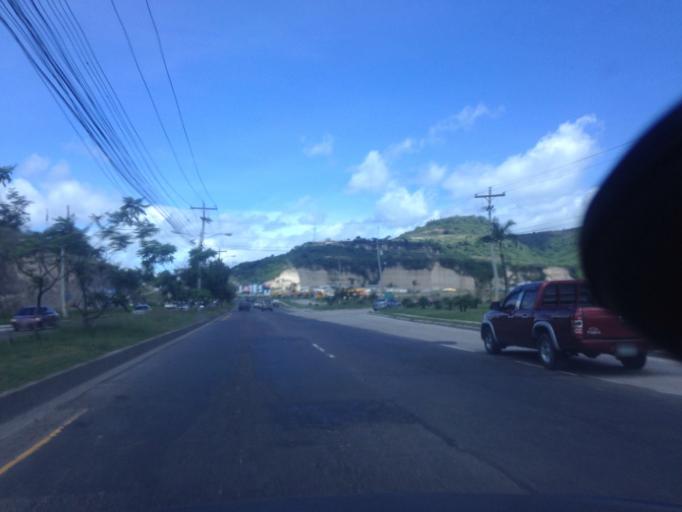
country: HN
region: Francisco Morazan
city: Tegucigalpa
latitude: 14.0500
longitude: -87.2012
